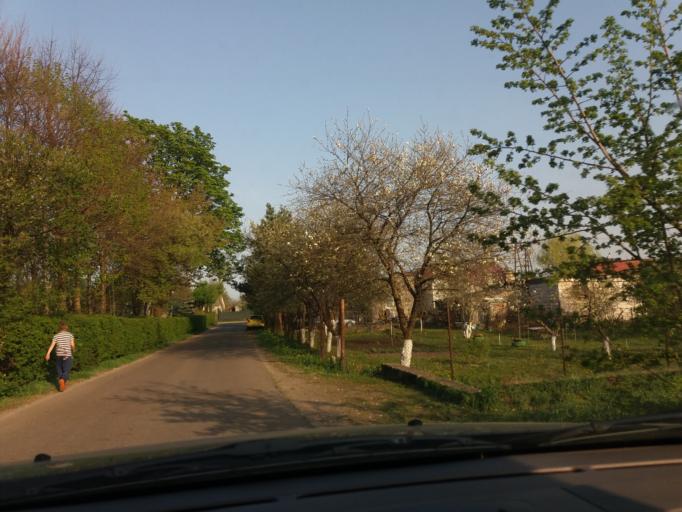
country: PL
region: Masovian Voivodeship
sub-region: Powiat mlawski
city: Mlawa
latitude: 53.1253
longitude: 20.3450
